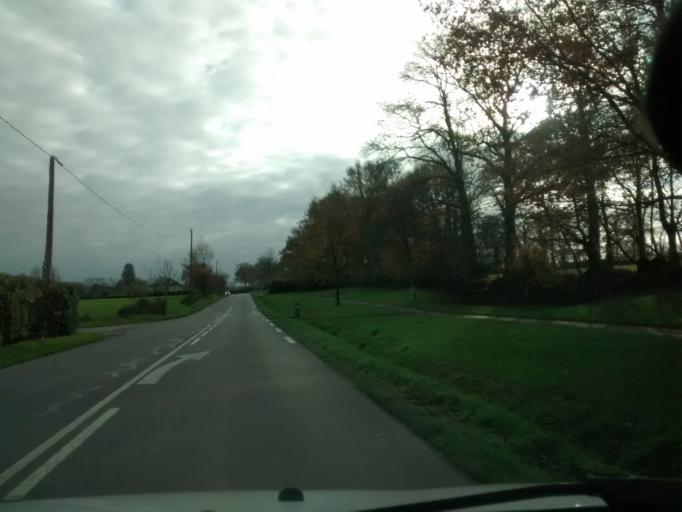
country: FR
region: Brittany
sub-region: Departement d'Ille-et-Vilaine
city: Montreuil-sous-Perouse
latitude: 48.1372
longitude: -1.2379
